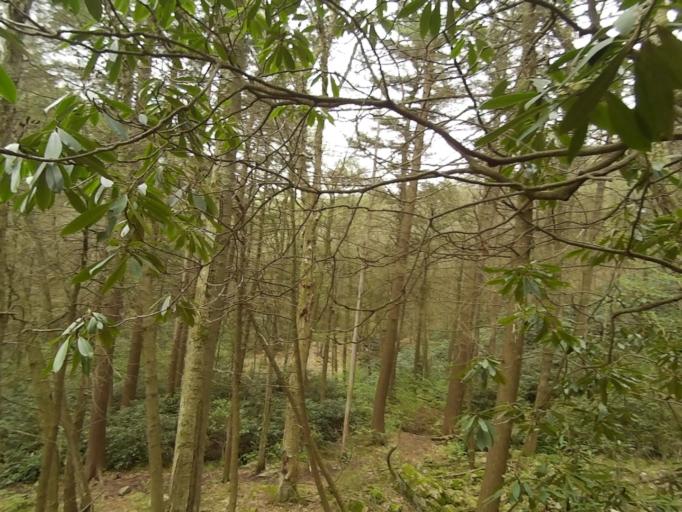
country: US
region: Pennsylvania
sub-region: Centre County
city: Boalsburg
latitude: 40.7517
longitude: -77.8182
